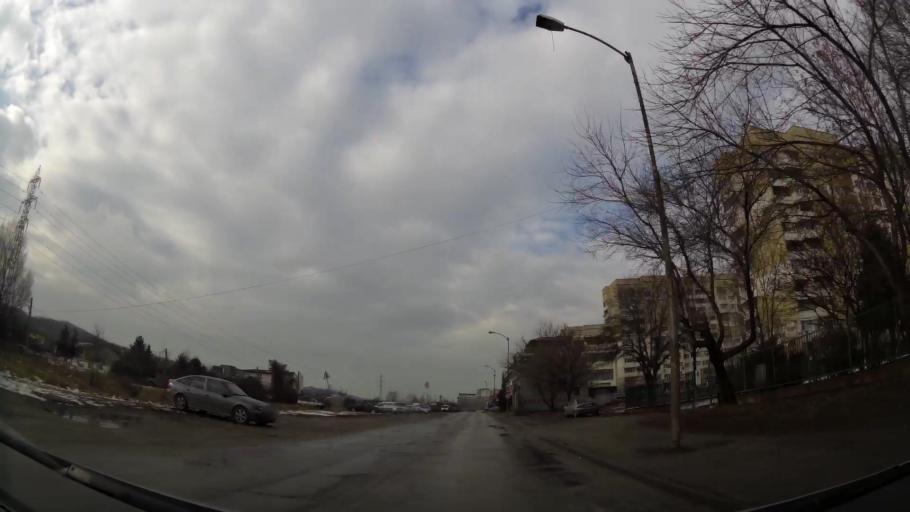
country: BG
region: Sofia-Capital
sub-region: Stolichna Obshtina
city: Sofia
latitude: 42.7098
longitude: 23.2640
